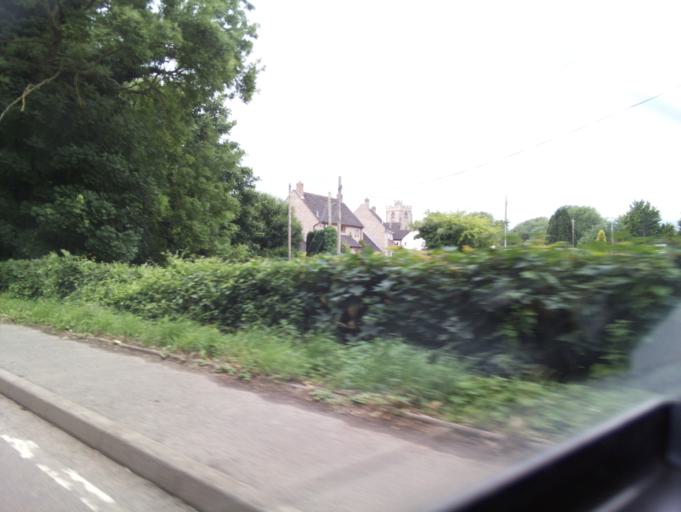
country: GB
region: England
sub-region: Worcestershire
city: Upton upon Severn
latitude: 52.0952
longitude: -2.2100
